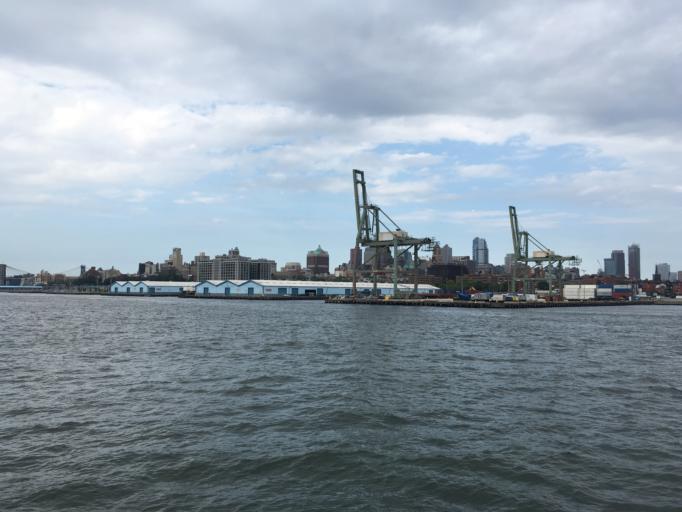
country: US
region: New York
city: New York City
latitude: 40.6886
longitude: -74.0095
